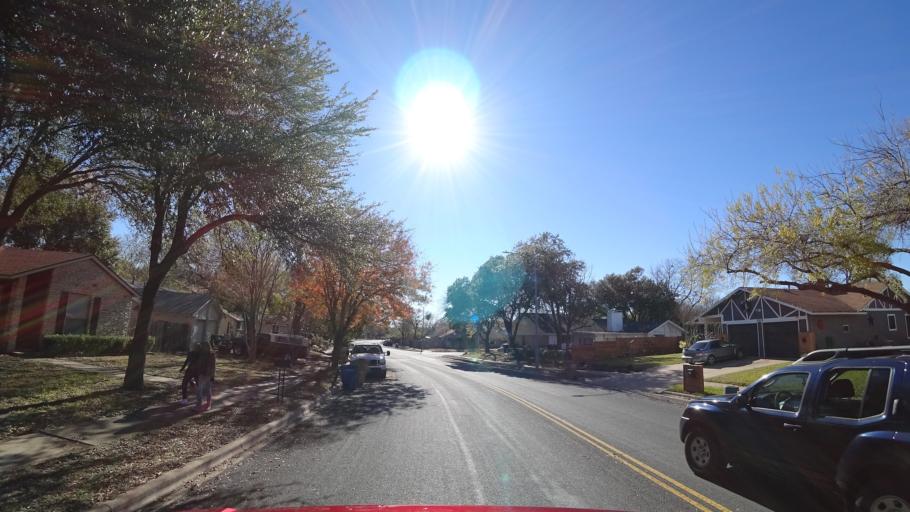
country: US
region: Texas
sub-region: Travis County
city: Wells Branch
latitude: 30.4209
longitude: -97.6938
